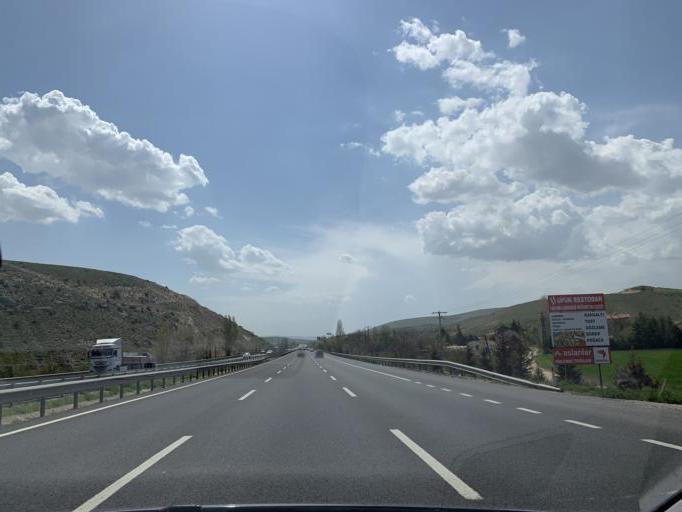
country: TR
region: Ankara
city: Temelli
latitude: 39.7837
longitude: 32.5131
